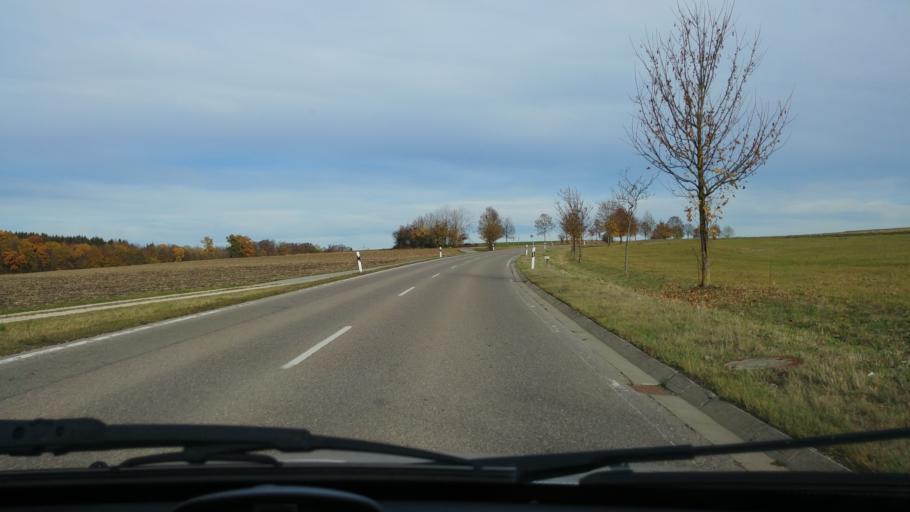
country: DE
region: Baden-Wuerttemberg
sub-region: Regierungsbezirk Stuttgart
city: Nattheim
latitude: 48.6754
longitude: 10.2343
